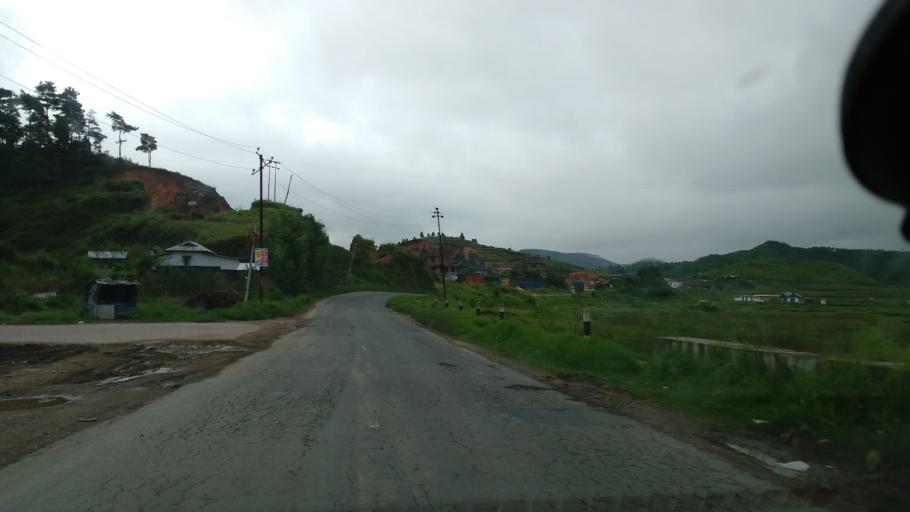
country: IN
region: Meghalaya
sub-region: East Khasi Hills
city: Shillong
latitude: 25.5102
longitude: 91.8117
